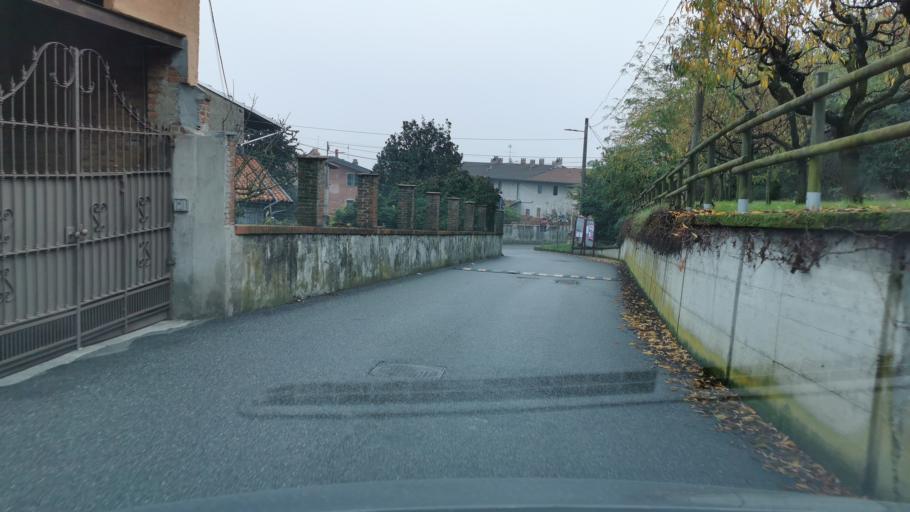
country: IT
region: Piedmont
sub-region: Provincia di Torino
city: Scarmagno
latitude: 45.3847
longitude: 7.8388
